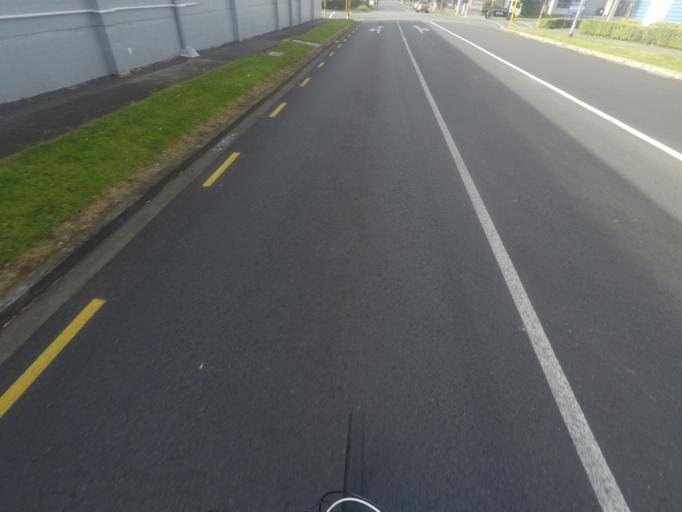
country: NZ
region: Auckland
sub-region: Auckland
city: Mangere
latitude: -36.9226
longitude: 174.7831
